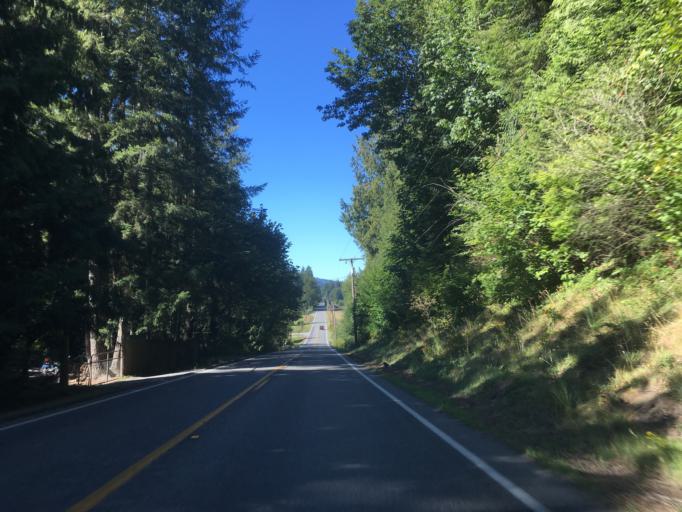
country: US
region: Washington
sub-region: Skagit County
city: Sedro-Woolley
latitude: 48.5712
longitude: -122.2245
